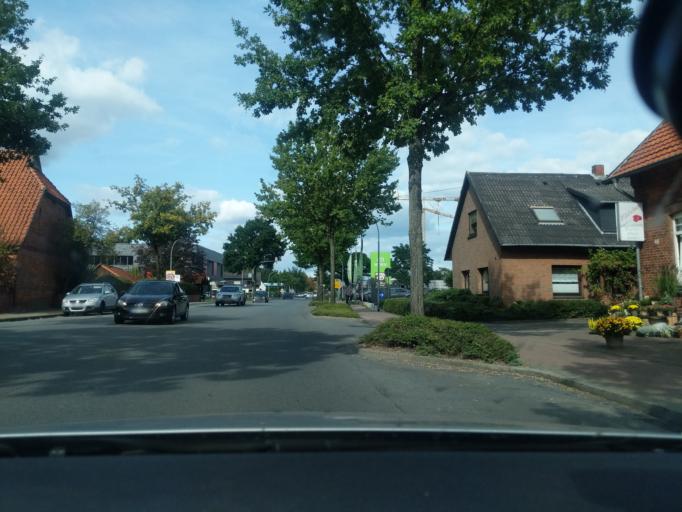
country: DE
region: Lower Saxony
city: Verden
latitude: 52.9456
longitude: 9.2328
